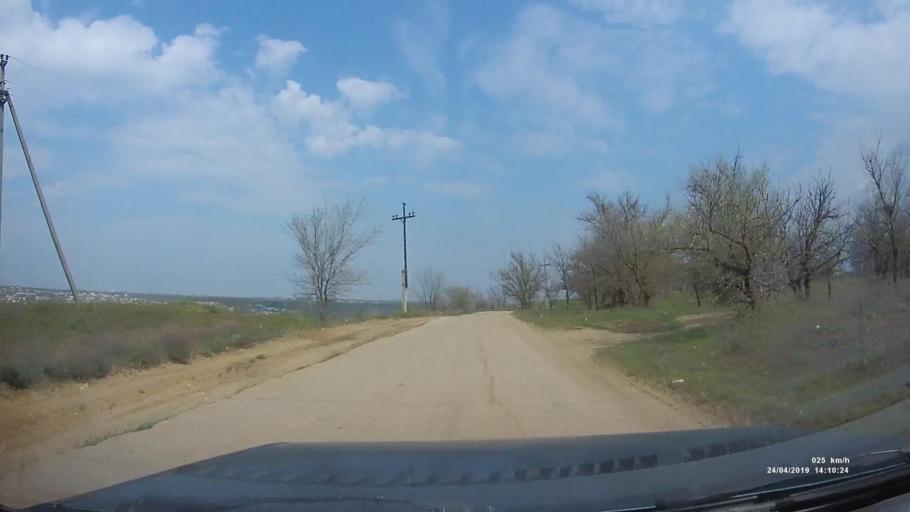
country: RU
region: Kalmykiya
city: Arshan'
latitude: 46.2646
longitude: 44.2270
